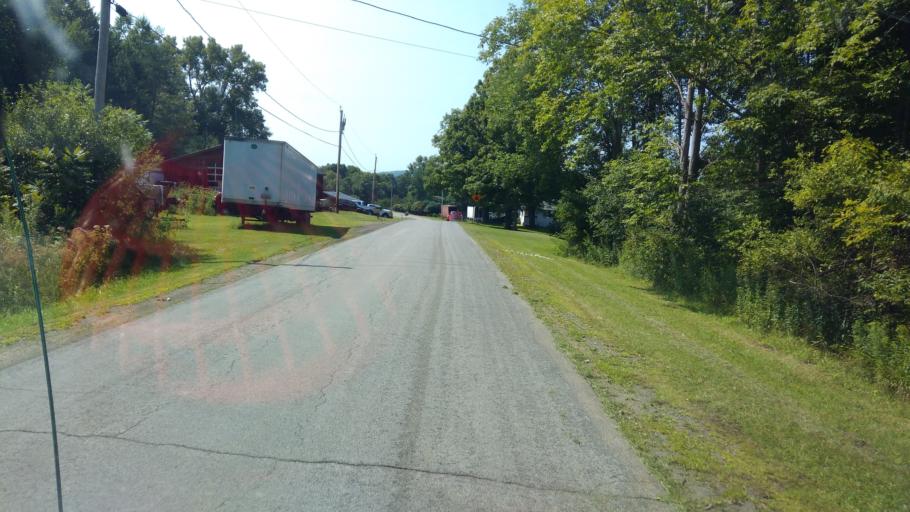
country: US
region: New York
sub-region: Allegany County
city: Belmont
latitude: 42.2427
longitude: -78.0150
